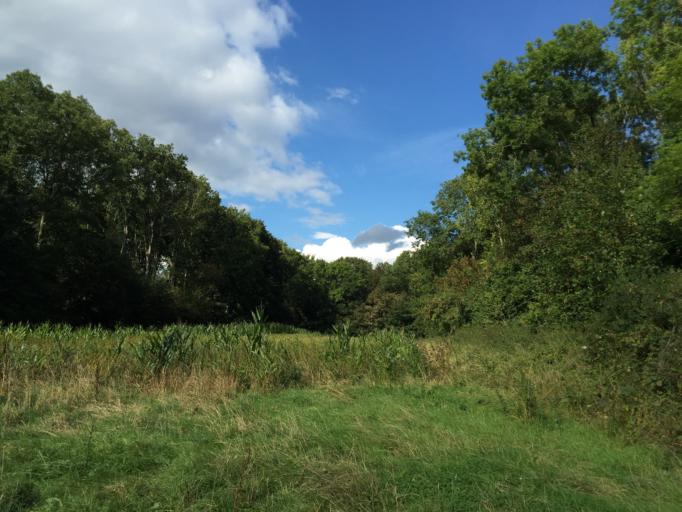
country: DK
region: South Denmark
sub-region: Sonderborg Kommune
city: Nordborg
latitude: 55.0117
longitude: 9.7497
